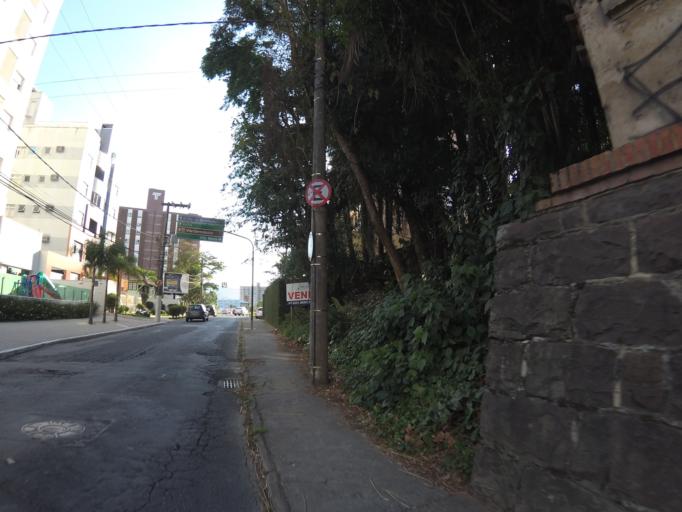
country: BR
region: Santa Catarina
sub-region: Blumenau
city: Blumenau
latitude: -26.9083
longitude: -49.0761
